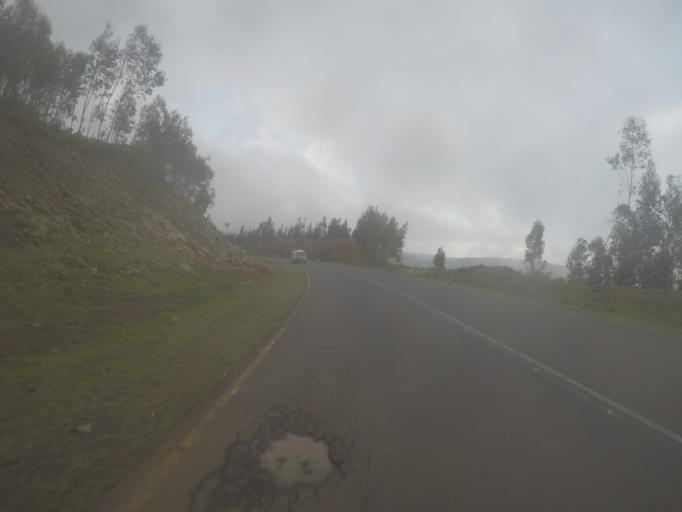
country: ET
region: Amhara
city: Gondar
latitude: 12.7298
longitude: 37.5157
